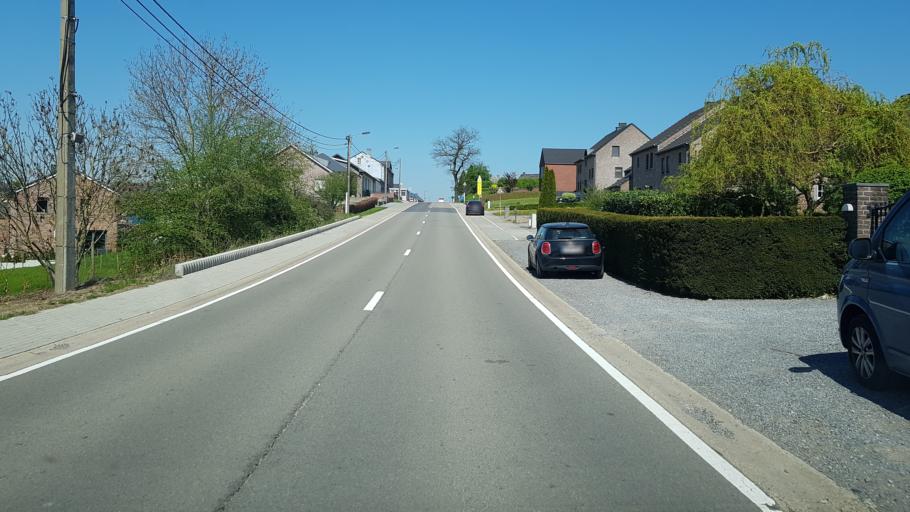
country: BE
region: Wallonia
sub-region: Province de Liege
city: Plombieres
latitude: 50.7208
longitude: 5.9187
